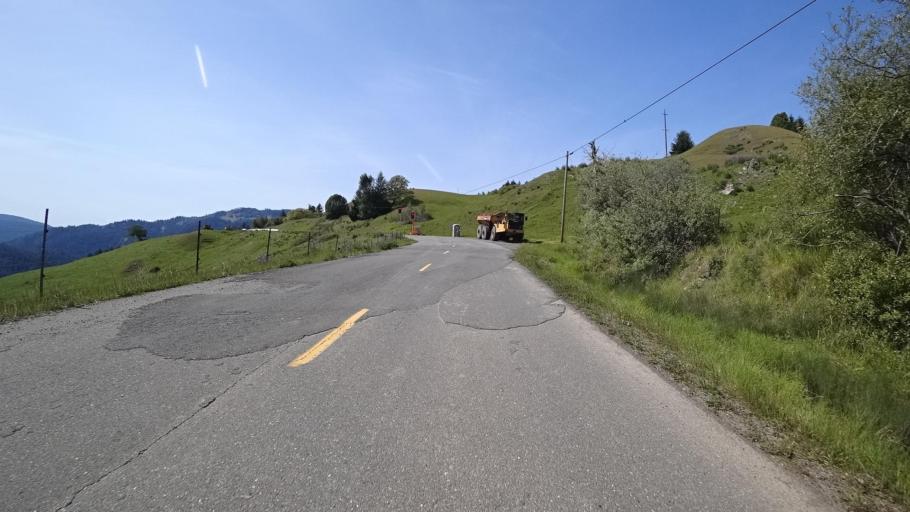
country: US
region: California
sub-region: Humboldt County
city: Redway
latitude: 40.4055
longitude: -123.7472
